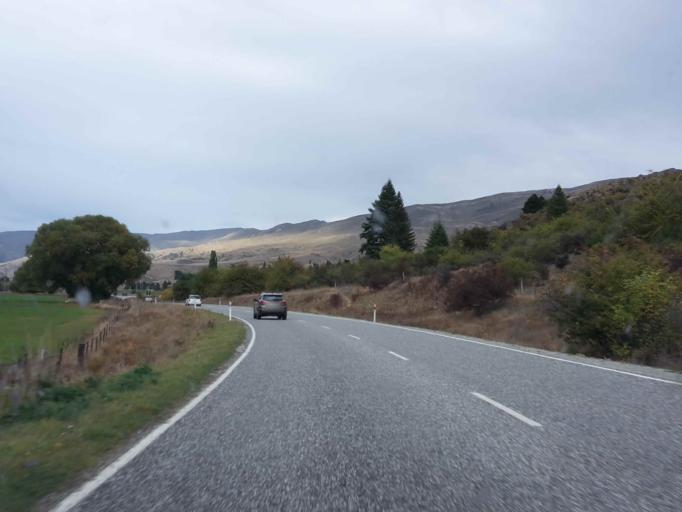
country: NZ
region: Otago
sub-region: Queenstown-Lakes District
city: Wanaka
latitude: -44.8527
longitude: 169.0357
